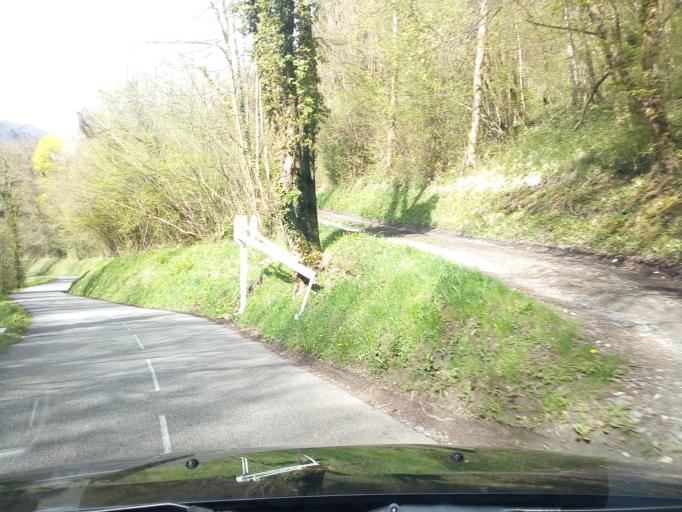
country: FR
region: Rhone-Alpes
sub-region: Departement de l'Isere
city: Domene
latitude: 45.1651
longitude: 5.8284
